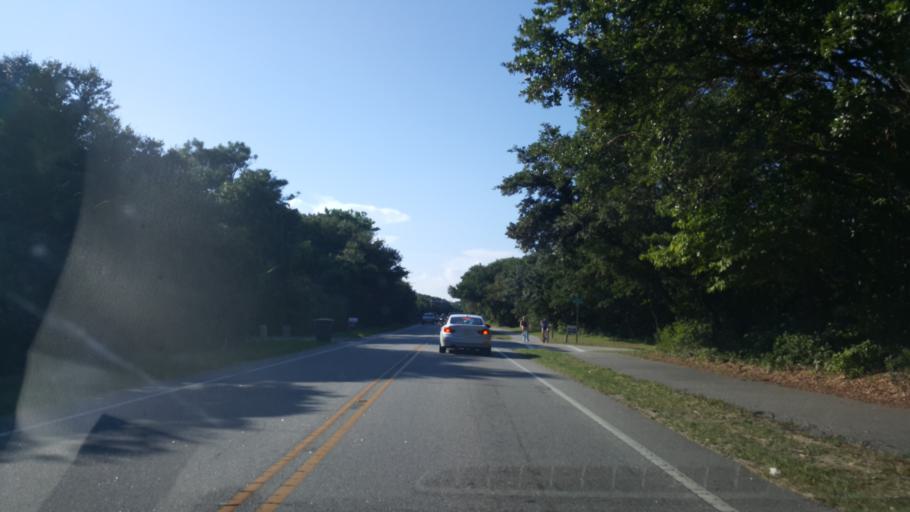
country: US
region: North Carolina
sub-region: Dare County
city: Southern Shores
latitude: 36.1421
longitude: -75.7382
